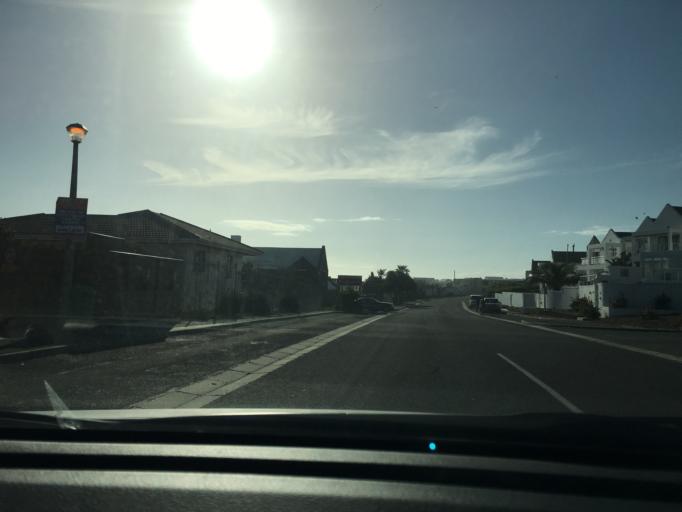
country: ZA
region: Western Cape
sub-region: City of Cape Town
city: Sunset Beach
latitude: -33.7956
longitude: 18.4593
